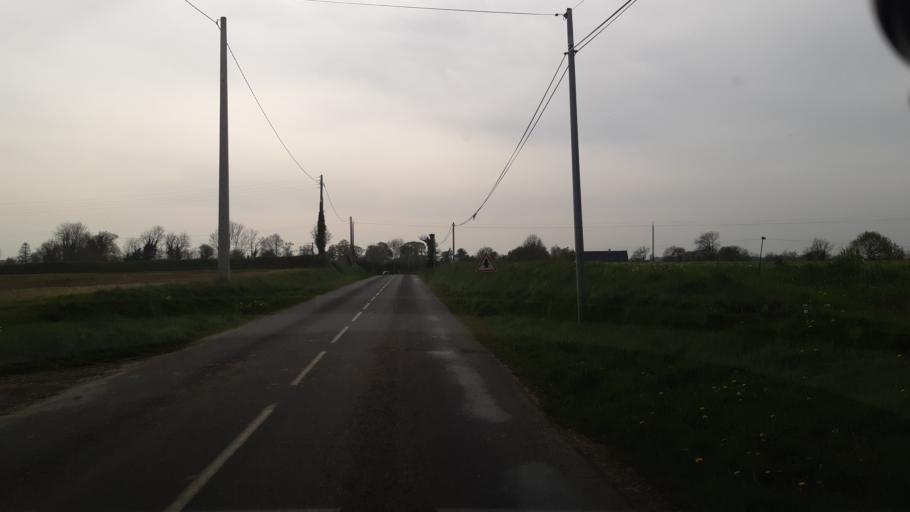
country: FR
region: Lower Normandy
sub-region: Departement de la Manche
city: Hambye
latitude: 48.9560
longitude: -1.3142
